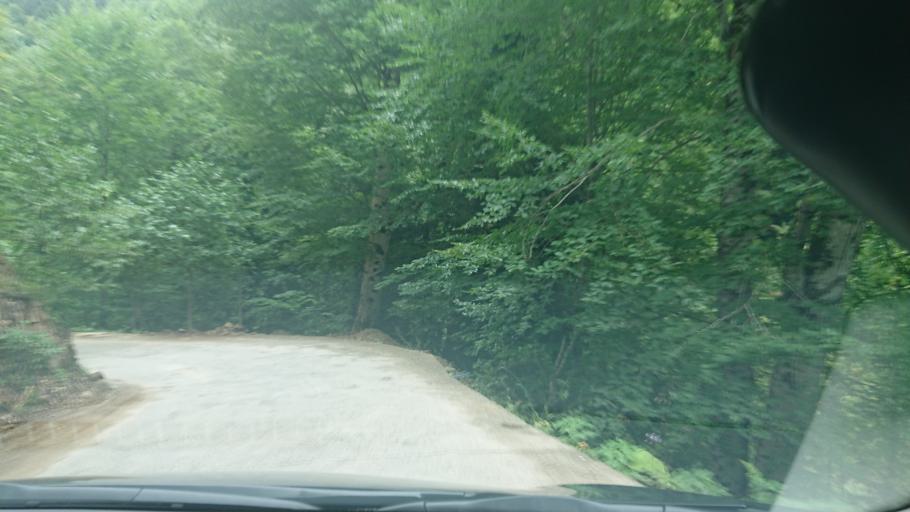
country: TR
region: Gumushane
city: Kurtun
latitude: 40.6702
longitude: 39.0429
